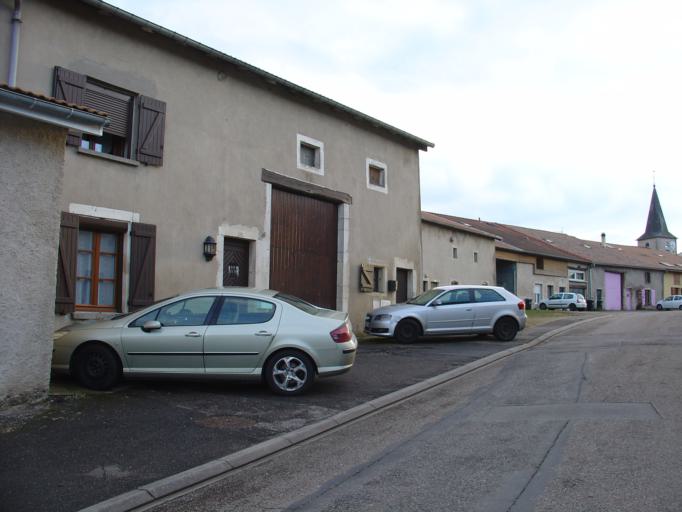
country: FR
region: Lorraine
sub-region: Departement de Meurthe-et-Moselle
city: Villey-Saint-Etienne
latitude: 48.7572
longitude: 5.9709
